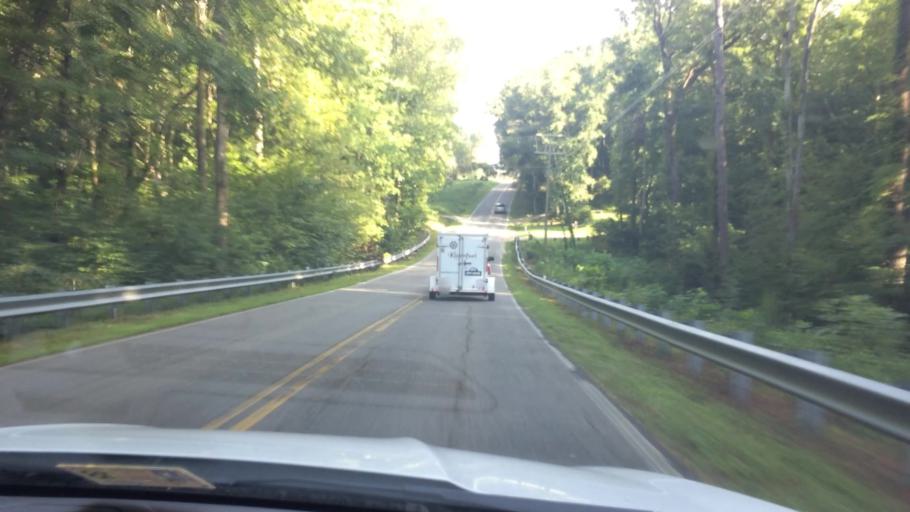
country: US
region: Virginia
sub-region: Middlesex County
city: Deltaville
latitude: 37.5651
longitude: -76.4522
